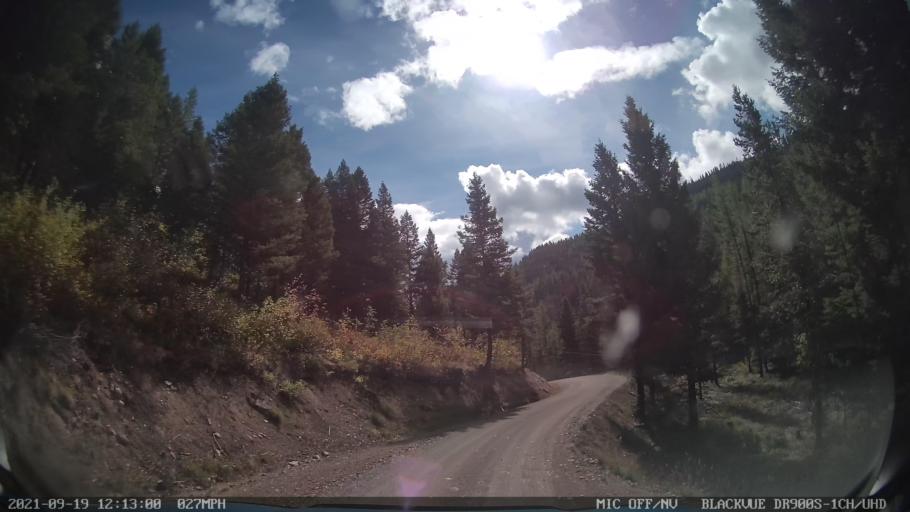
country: US
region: Montana
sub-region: Missoula County
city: Seeley Lake
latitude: 47.1696
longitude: -113.3606
